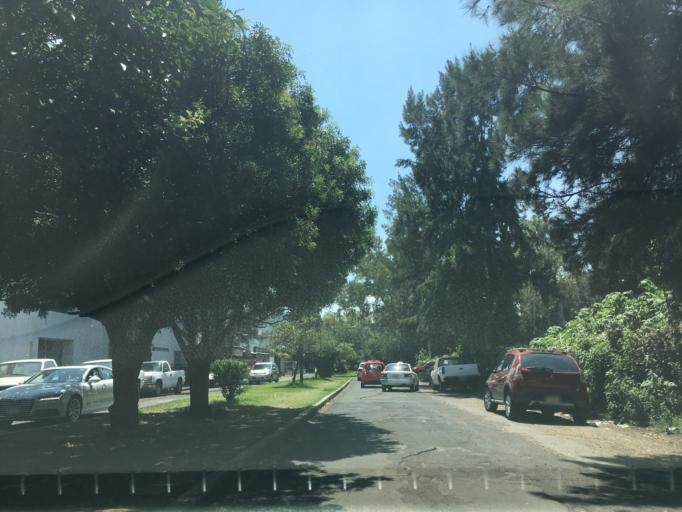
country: MX
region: Michoacan
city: Morelia
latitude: 19.6899
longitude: -101.1801
